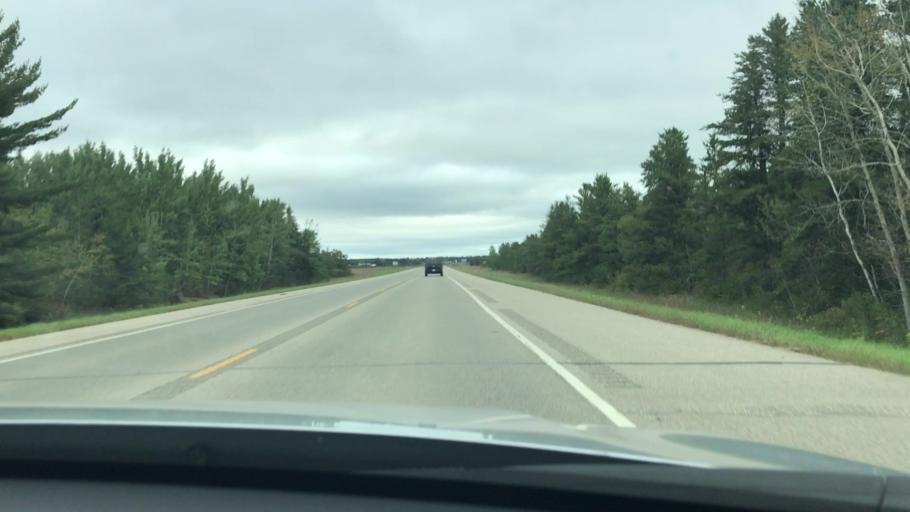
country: US
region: Minnesota
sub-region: Hubbard County
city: Park Rapids
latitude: 46.8510
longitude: -95.0787
